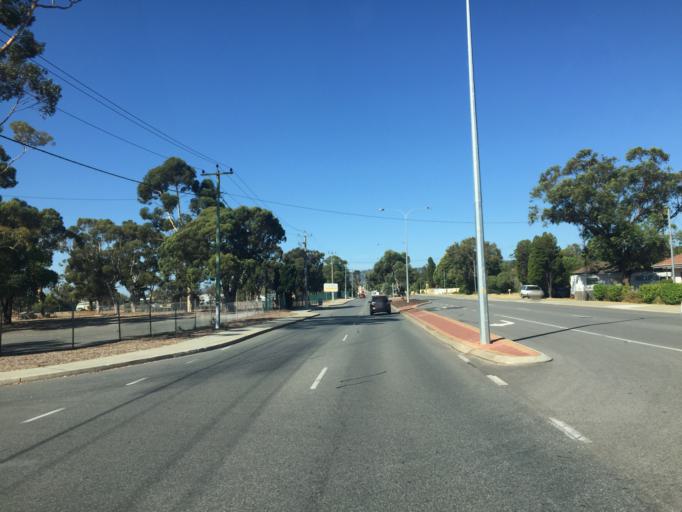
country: AU
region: Western Australia
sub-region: Gosnells
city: Maddington
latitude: -32.0489
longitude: 115.9851
